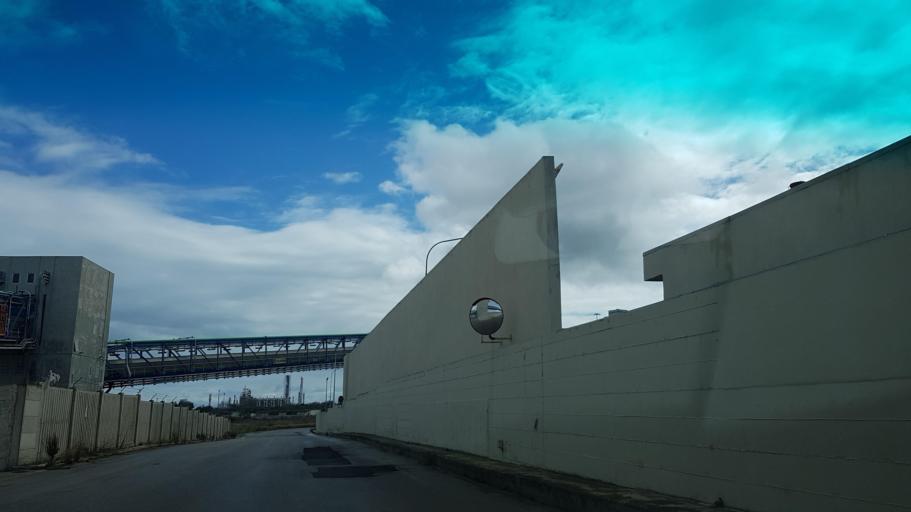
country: IT
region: Apulia
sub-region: Provincia di Brindisi
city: Materdomini
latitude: 40.6453
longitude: 17.9797
